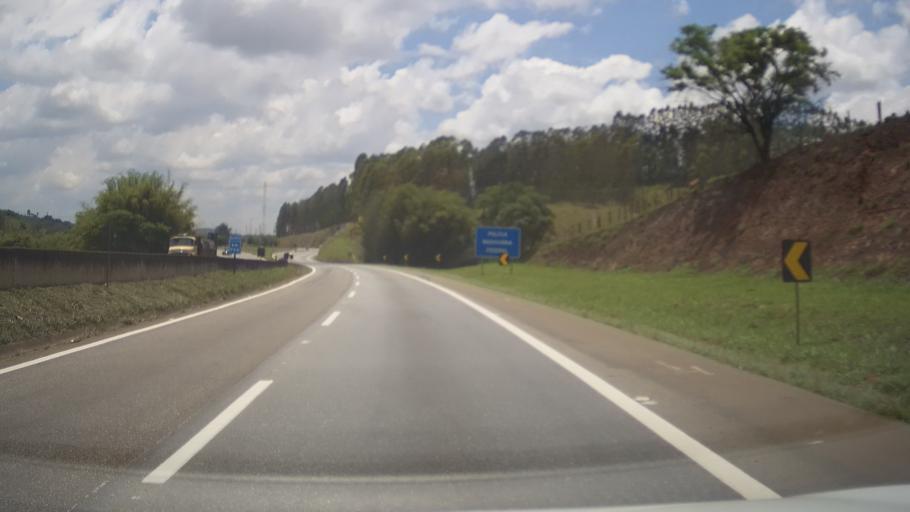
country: BR
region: Minas Gerais
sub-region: Tres Coracoes
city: Tres Coracoes
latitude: -21.6936
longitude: -45.3527
